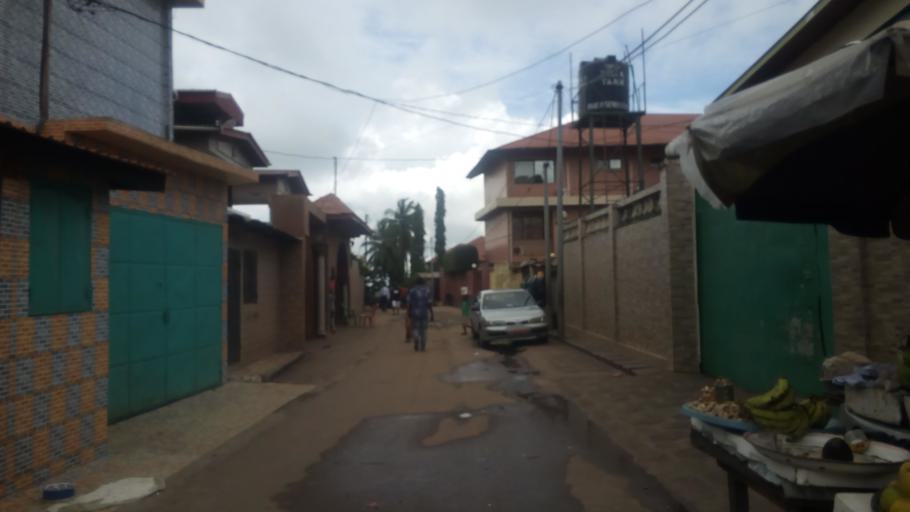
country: GN
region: Conakry
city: Conakry
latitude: 9.5986
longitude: -13.6538
